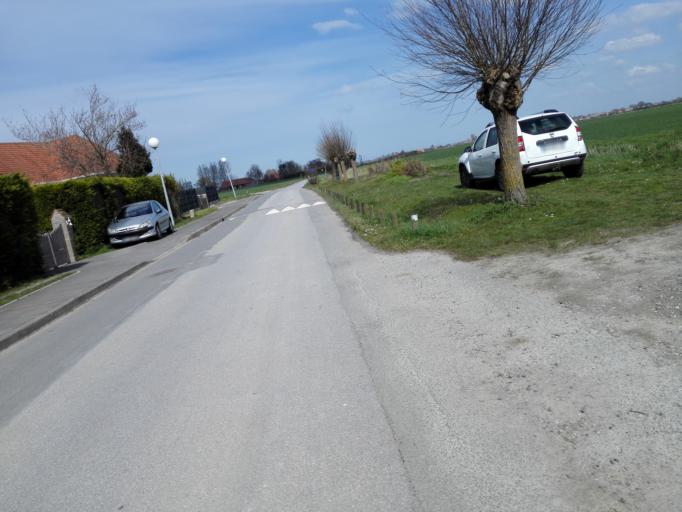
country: FR
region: Nord-Pas-de-Calais
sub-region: Departement du Nord
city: Brouckerque
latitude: 50.9579
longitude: 2.2955
